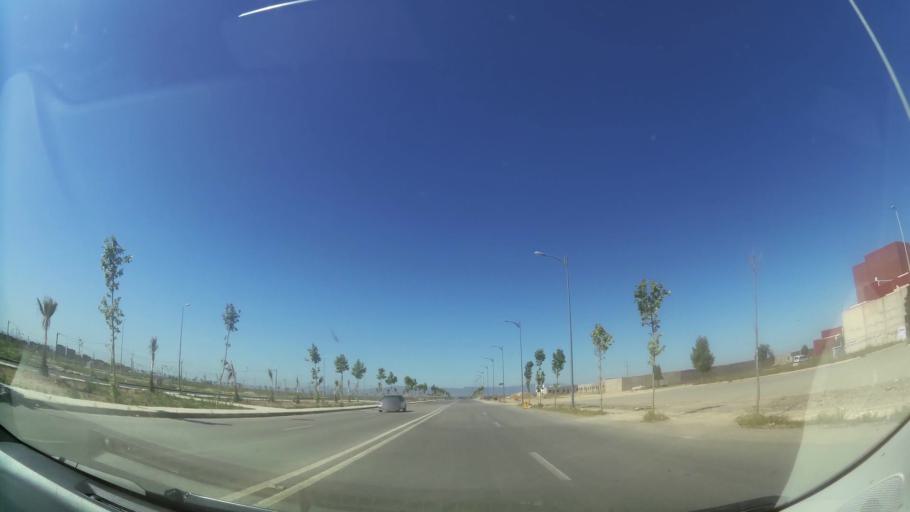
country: MA
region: Oriental
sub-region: Oujda-Angad
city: Oujda
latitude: 34.6811
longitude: -1.8588
